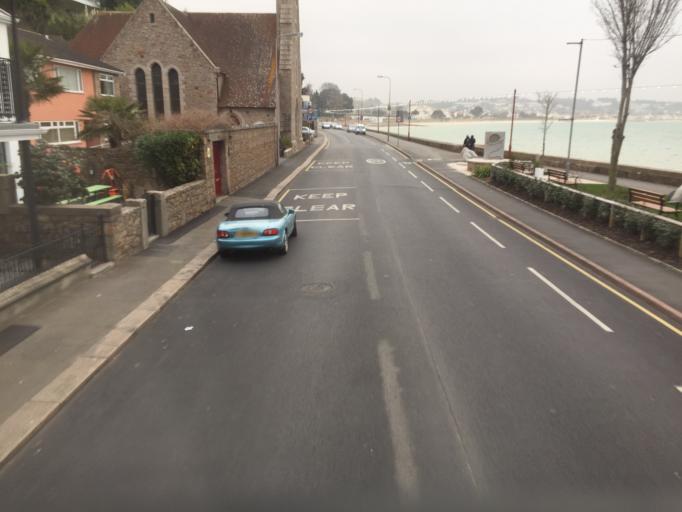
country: JE
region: St Helier
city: Saint Helier
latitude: 49.1888
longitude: -2.1694
